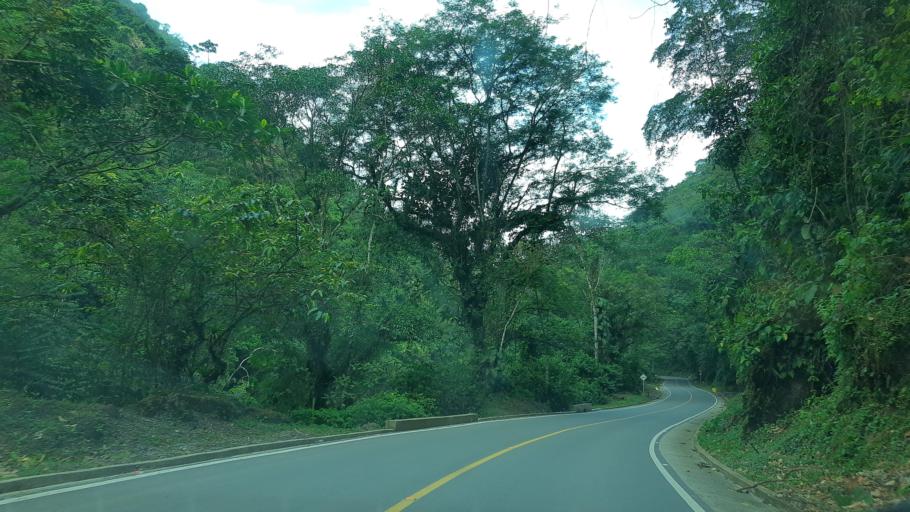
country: CO
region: Boyaca
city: Santa Maria
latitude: 4.8459
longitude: -73.2254
